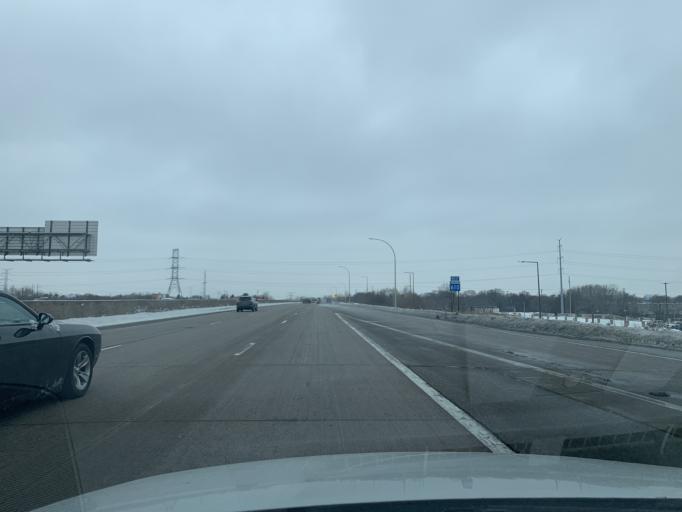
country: US
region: Minnesota
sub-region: Anoka County
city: Coon Rapids
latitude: 45.1415
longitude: -93.2840
